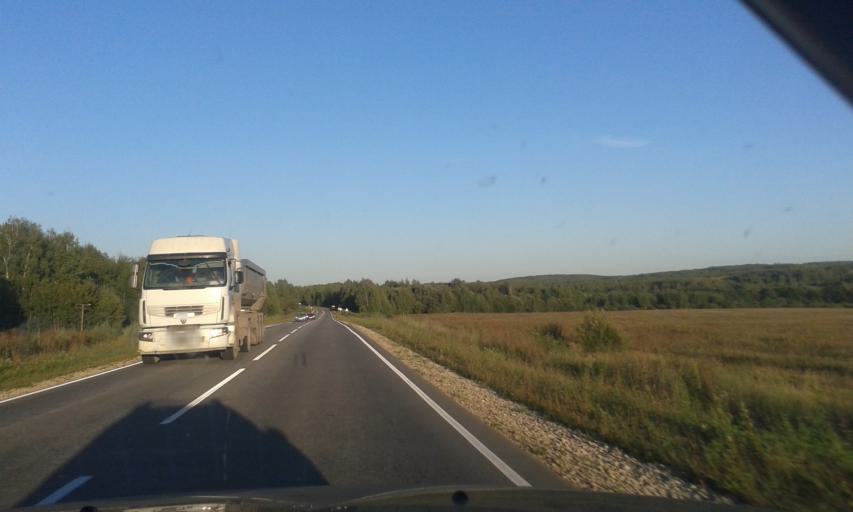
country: RU
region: Tula
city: Krapivna
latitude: 54.1139
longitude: 37.1944
